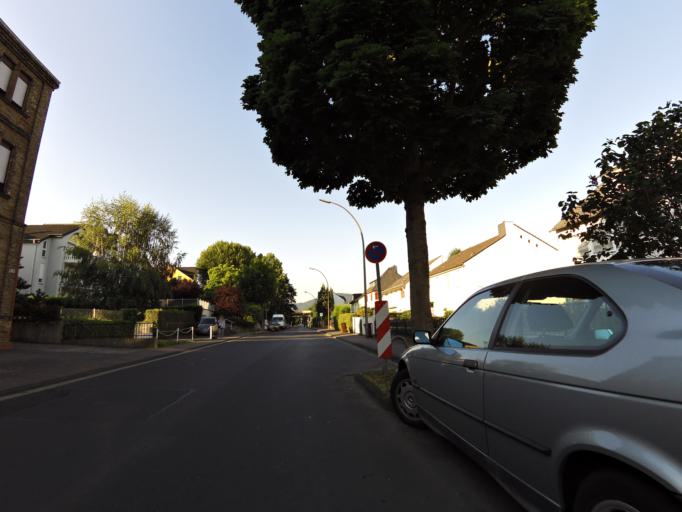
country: DE
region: Rheinland-Pfalz
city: Koblenz
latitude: 50.3338
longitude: 7.5986
